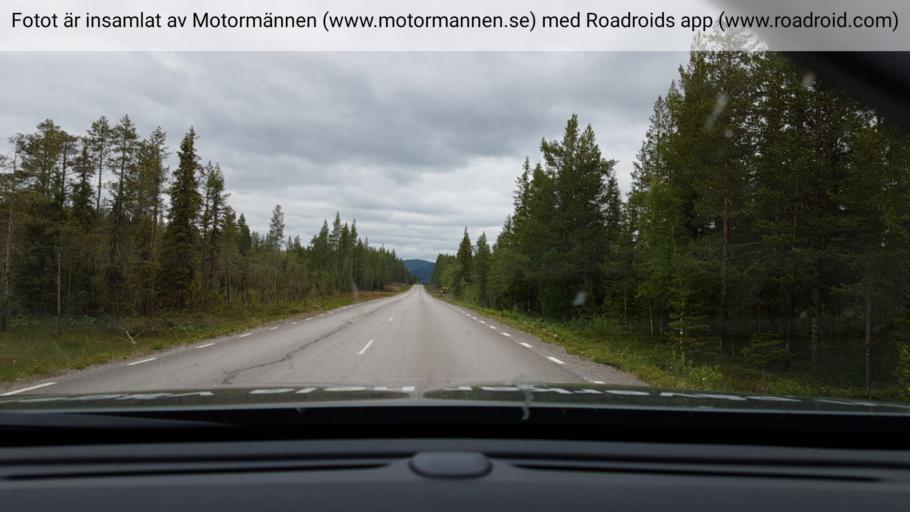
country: SE
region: Vaesterbotten
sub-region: Sorsele Kommun
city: Sorsele
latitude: 65.6160
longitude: 17.4906
